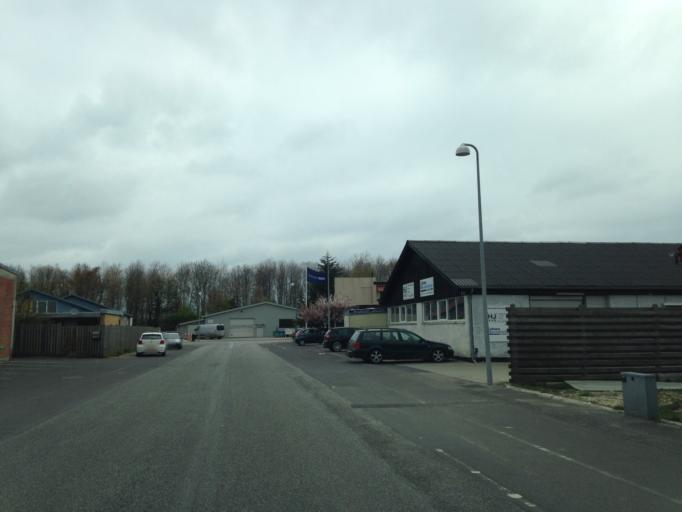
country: DK
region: Zealand
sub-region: Greve Kommune
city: Greve
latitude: 55.5903
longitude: 12.2957
